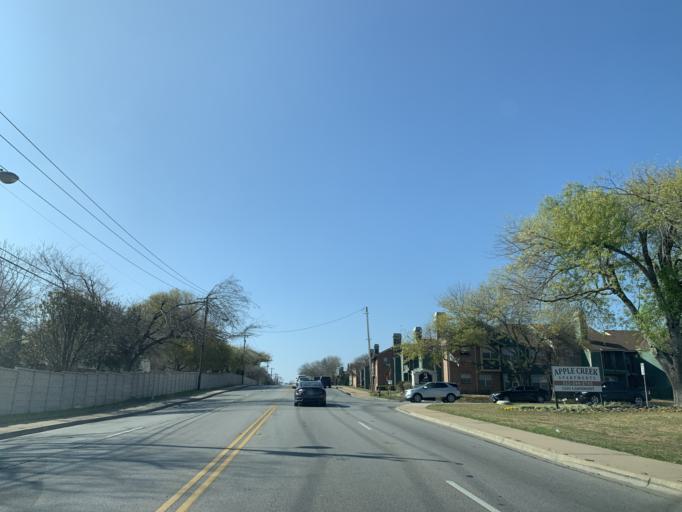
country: US
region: Texas
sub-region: Williamson County
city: Round Rock
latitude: 30.4956
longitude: -97.6687
